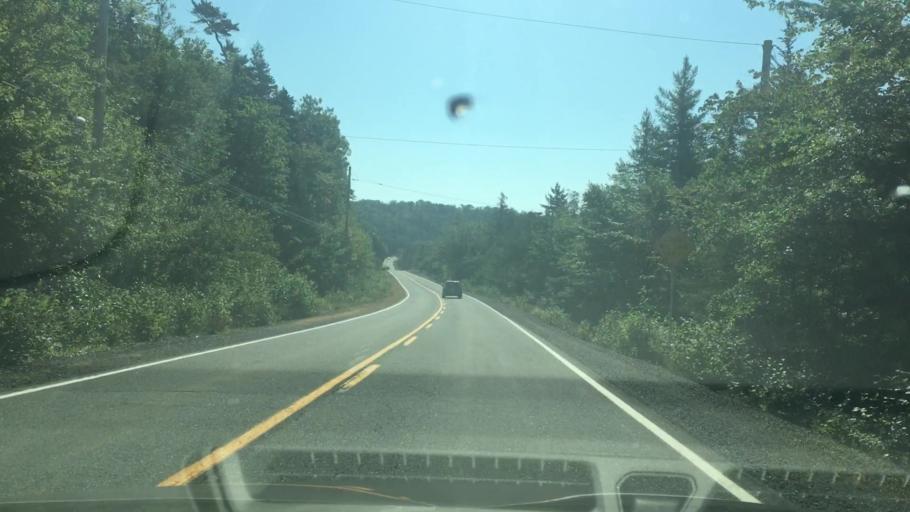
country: CA
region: Nova Scotia
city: Cole Harbour
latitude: 44.8070
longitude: -62.8323
